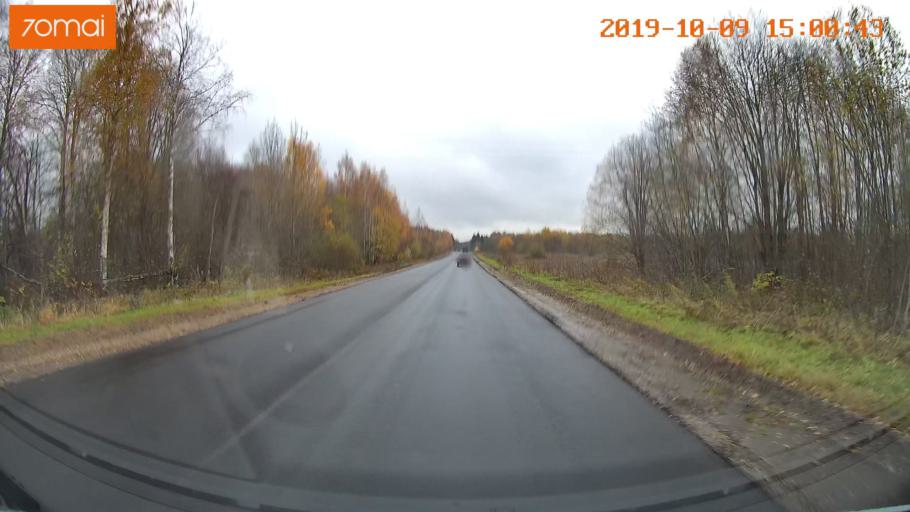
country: RU
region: Kostroma
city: Chistyye Bory
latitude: 58.3061
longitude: 41.6787
